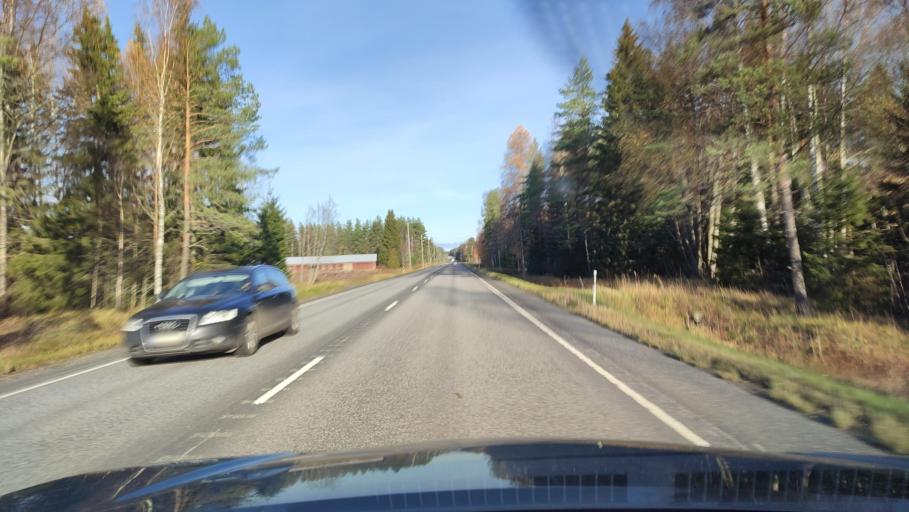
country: FI
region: Ostrobothnia
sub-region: Vaasa
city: Malax
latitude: 62.8024
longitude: 21.6776
